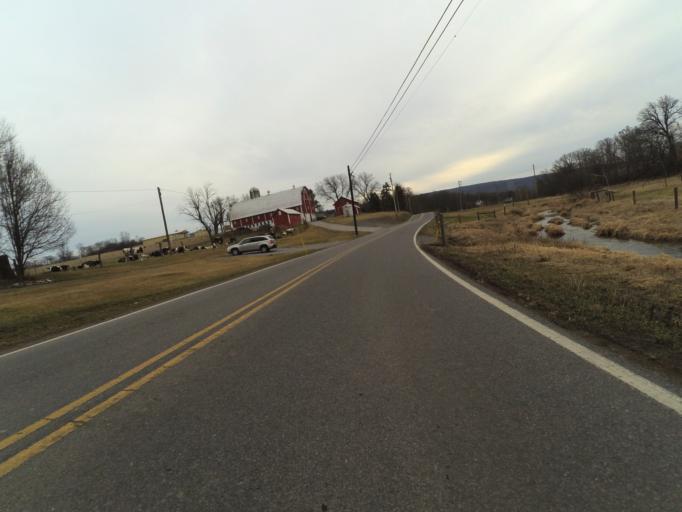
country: US
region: Pennsylvania
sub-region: Centre County
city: State College
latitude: 40.7823
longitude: -77.8314
